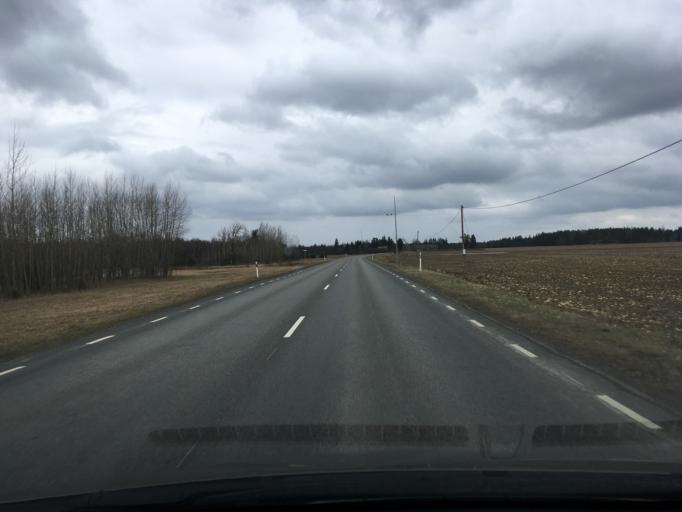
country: EE
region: Laeaene
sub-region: Lihula vald
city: Lihula
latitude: 58.5855
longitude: 23.9741
